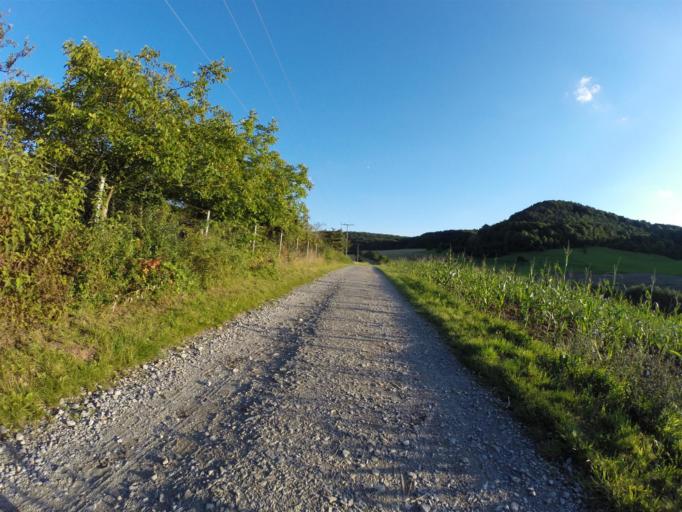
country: DE
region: Thuringia
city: Grosslobichau
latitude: 50.9247
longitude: 11.6463
